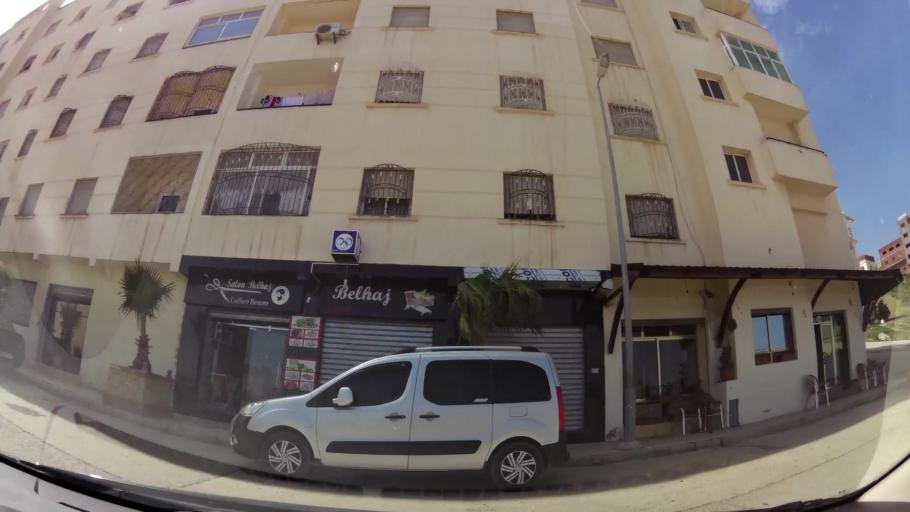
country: MA
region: Tanger-Tetouan
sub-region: Tanger-Assilah
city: Tangier
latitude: 35.7329
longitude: -5.8150
